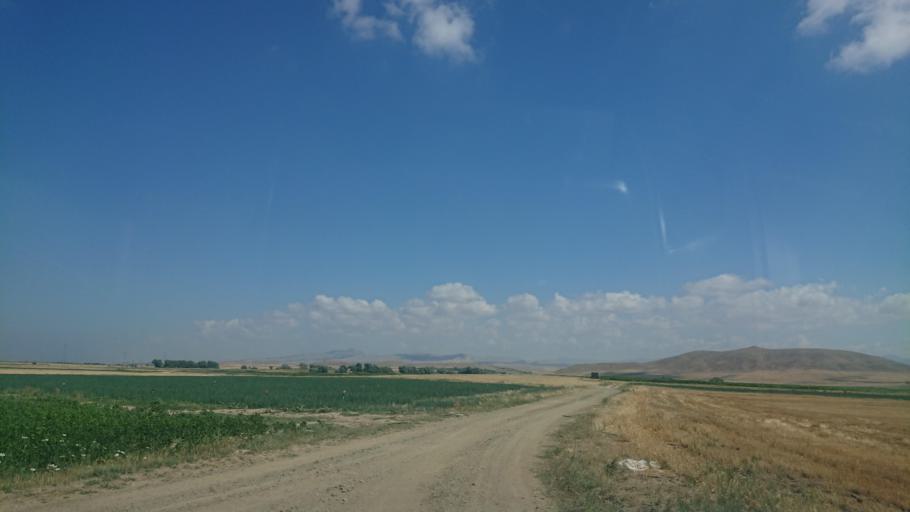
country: TR
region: Aksaray
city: Sariyahsi
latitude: 38.9880
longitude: 33.9023
